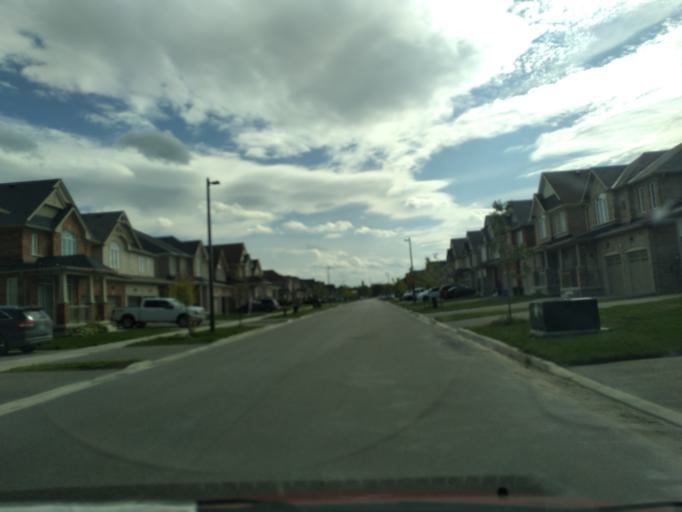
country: CA
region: Ontario
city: Keswick
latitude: 44.3051
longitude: -79.3773
